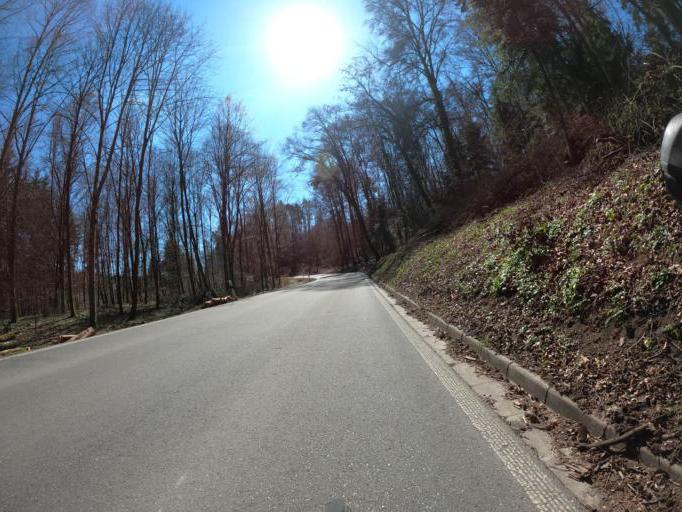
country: DE
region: Baden-Wuerttemberg
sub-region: Tuebingen Region
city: Haigerloch
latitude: 48.4389
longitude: 8.8060
